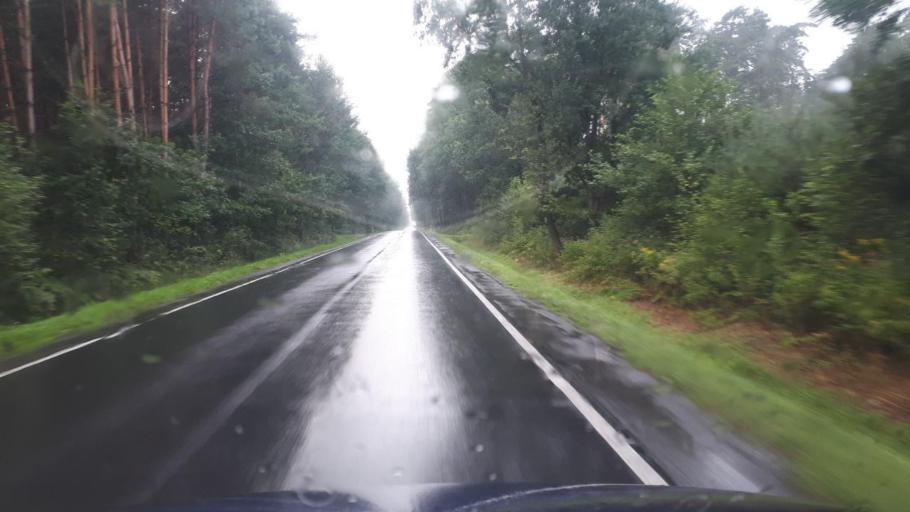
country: PL
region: Silesian Voivodeship
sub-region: Powiat tarnogorski
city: Tworog
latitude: 50.5294
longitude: 18.6694
